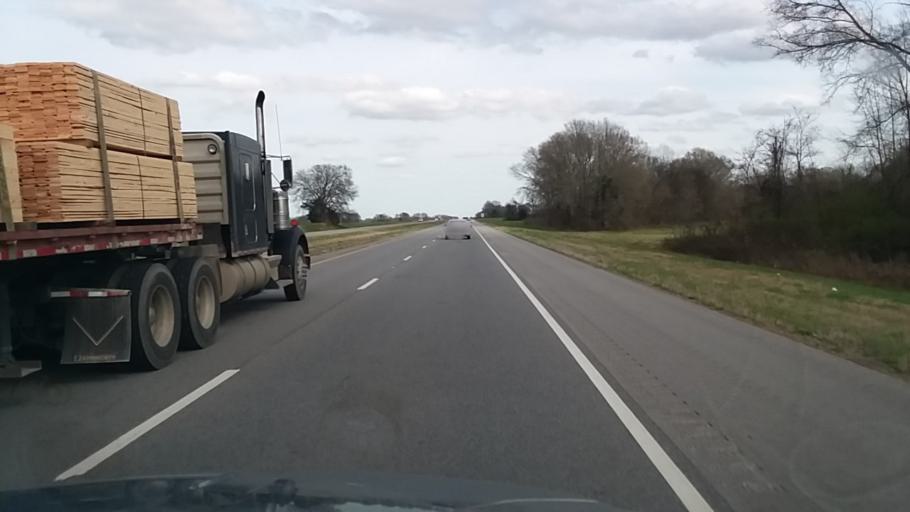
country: US
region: Alabama
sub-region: Lawrence County
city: Town Creek
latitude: 34.6840
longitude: -87.5420
